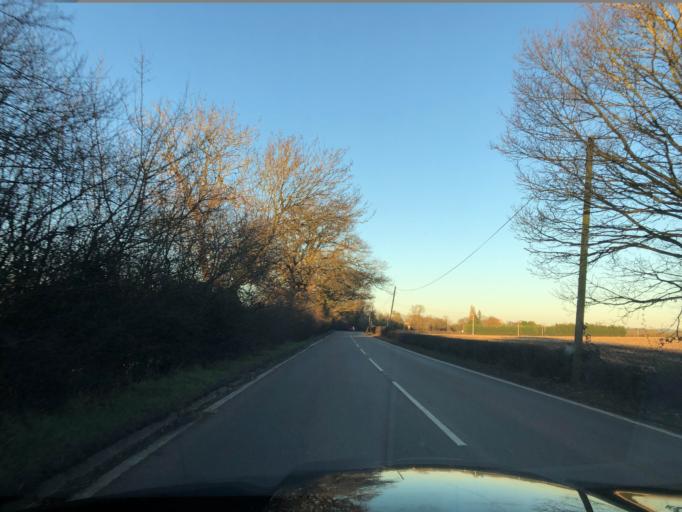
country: GB
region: England
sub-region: Warwickshire
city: Harbury
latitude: 52.2031
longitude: -1.4472
